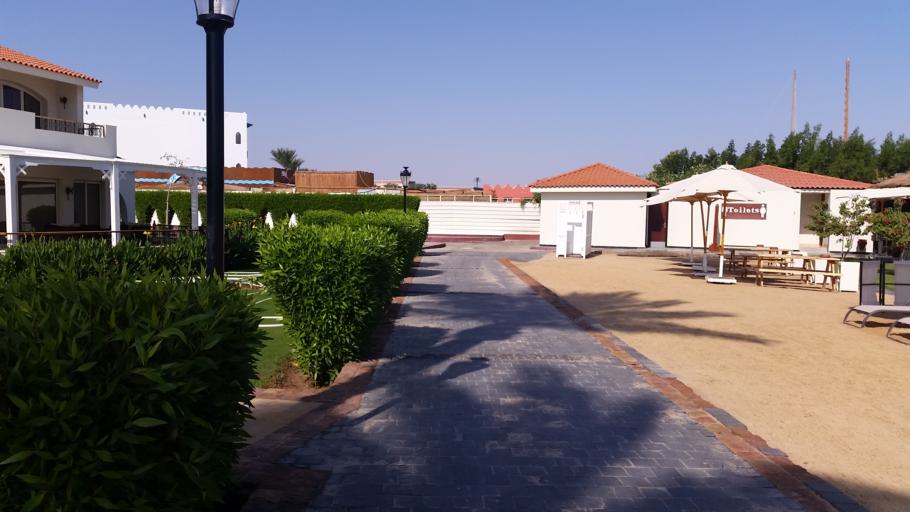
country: EG
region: Red Sea
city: Makadi Bay
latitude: 27.1012
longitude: 33.8341
